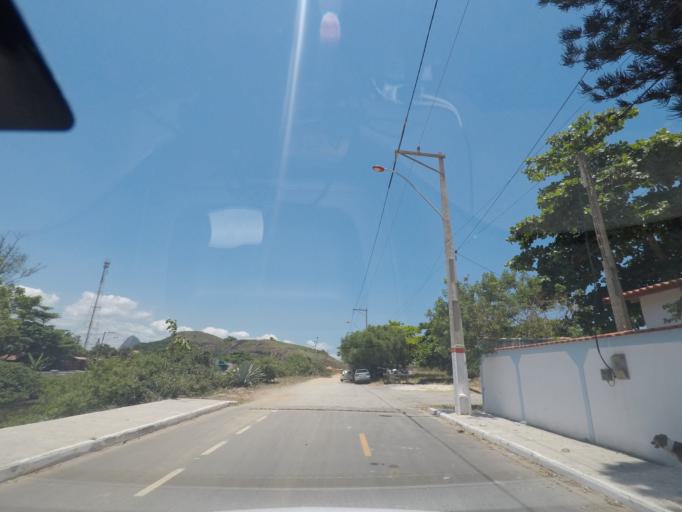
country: BR
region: Rio de Janeiro
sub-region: Niteroi
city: Niteroi
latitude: -22.9689
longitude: -43.0077
